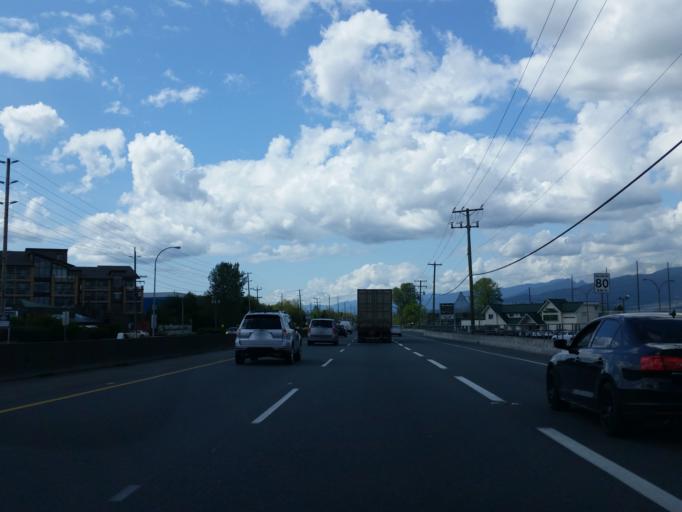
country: CA
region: British Columbia
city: Pitt Meadows
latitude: 49.2322
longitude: -122.6920
